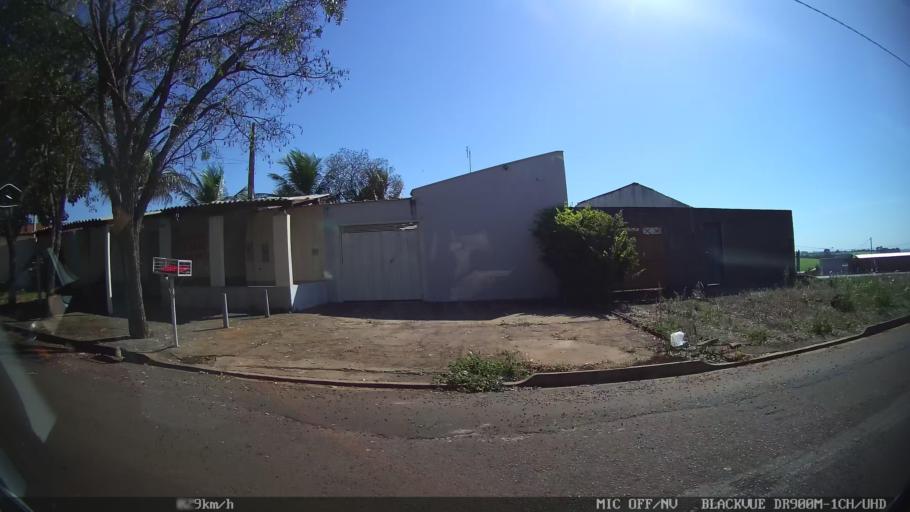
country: BR
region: Sao Paulo
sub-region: Batatais
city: Batatais
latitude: -20.8846
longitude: -47.5671
